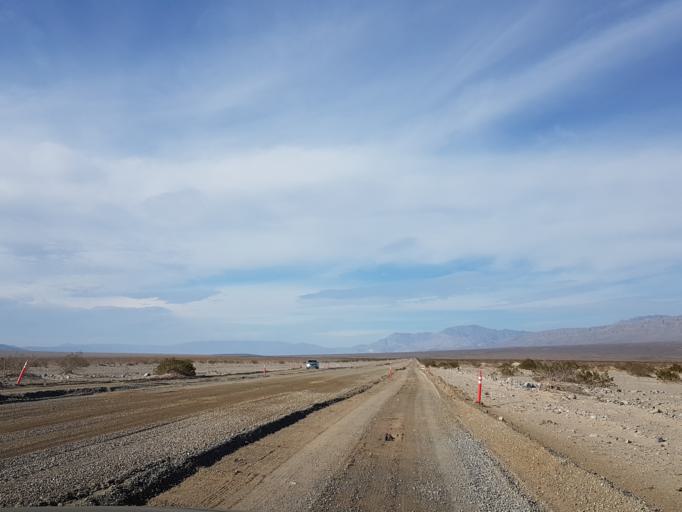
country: US
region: California
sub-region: San Bernardino County
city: Searles Valley
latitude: 36.1414
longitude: -117.2961
